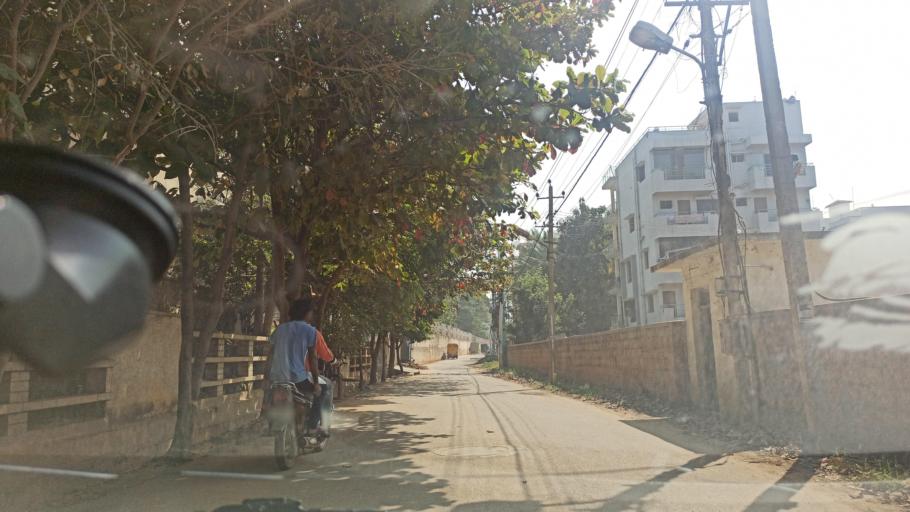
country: IN
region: Karnataka
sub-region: Bangalore Urban
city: Yelahanka
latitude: 13.0680
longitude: 77.5887
